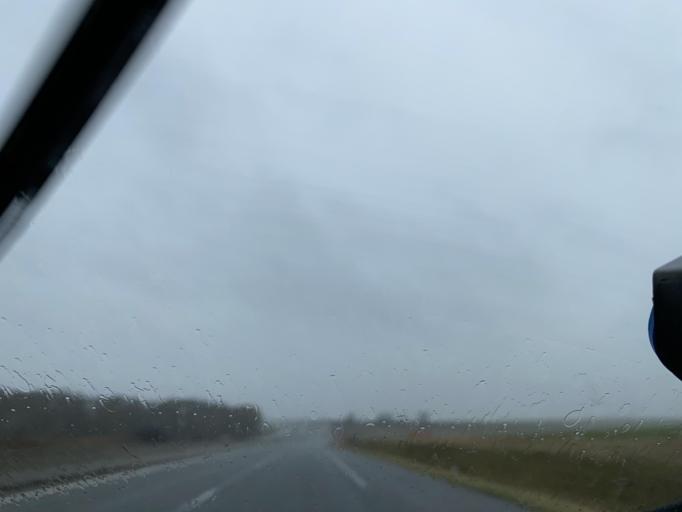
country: FR
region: Centre
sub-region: Departement d'Eure-et-Loir
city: Villemeux-sur-Eure
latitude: 48.6014
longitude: 1.4222
